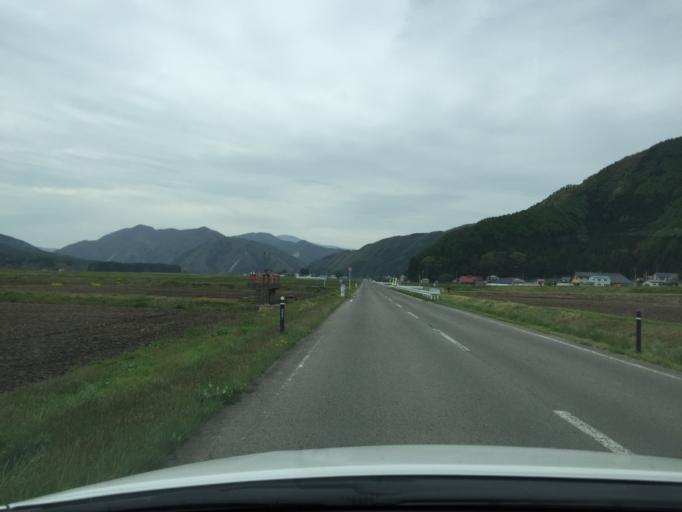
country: JP
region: Fukushima
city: Inawashiro
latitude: 37.5710
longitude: 140.1353
